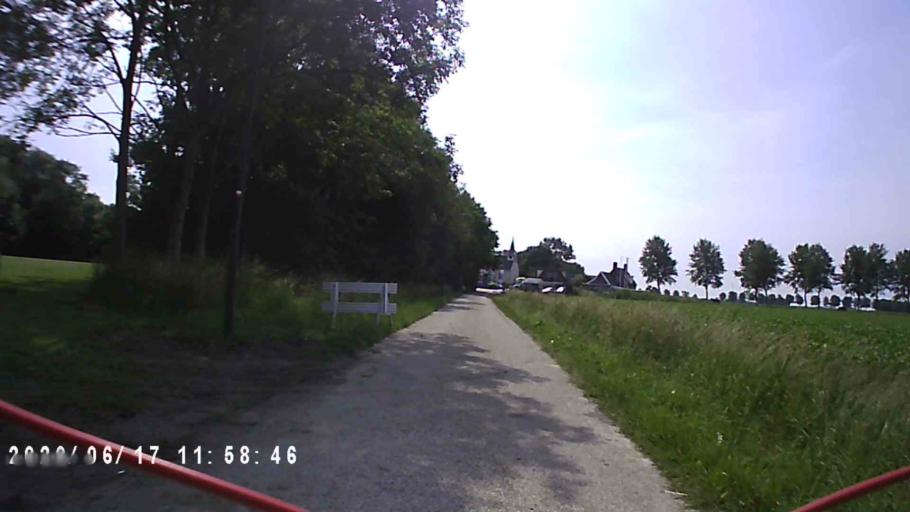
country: NL
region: Groningen
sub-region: Gemeente De Marne
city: Ulrum
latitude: 53.3437
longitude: 6.3283
